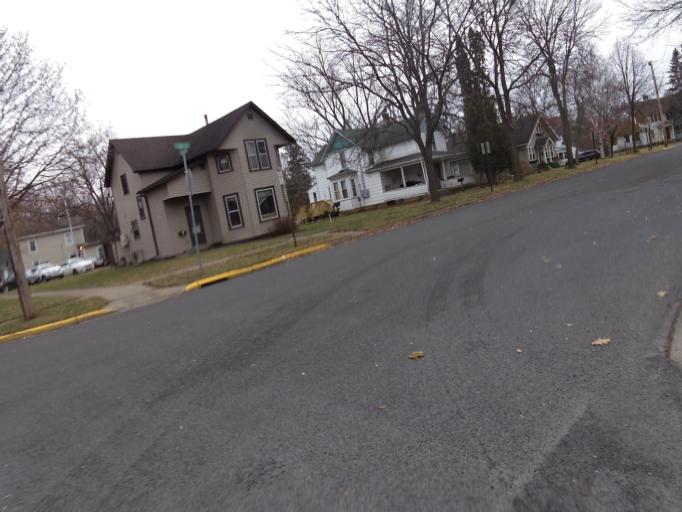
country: US
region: Wisconsin
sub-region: Pierce County
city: River Falls
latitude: 44.8561
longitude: -92.6211
